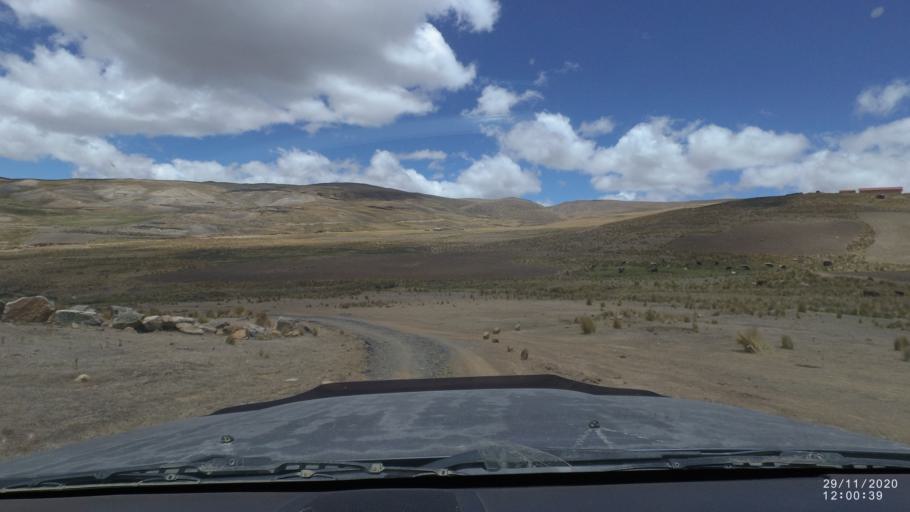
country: BO
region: Cochabamba
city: Cochabamba
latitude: -17.1520
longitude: -66.2788
